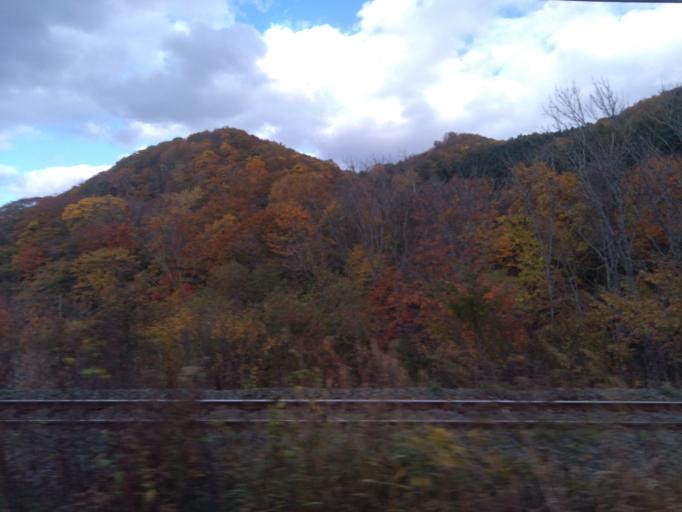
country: JP
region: Hokkaido
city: Niseko Town
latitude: 42.5957
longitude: 140.5877
